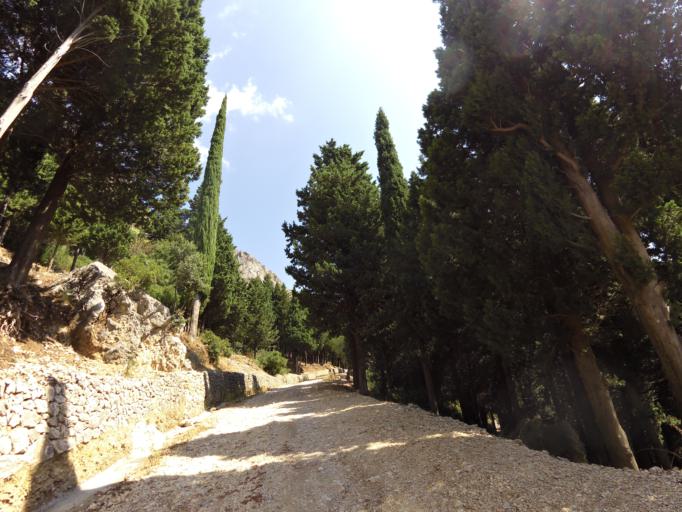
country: IT
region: Calabria
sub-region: Provincia di Reggio Calabria
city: Stilo
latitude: 38.4751
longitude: 16.4606
